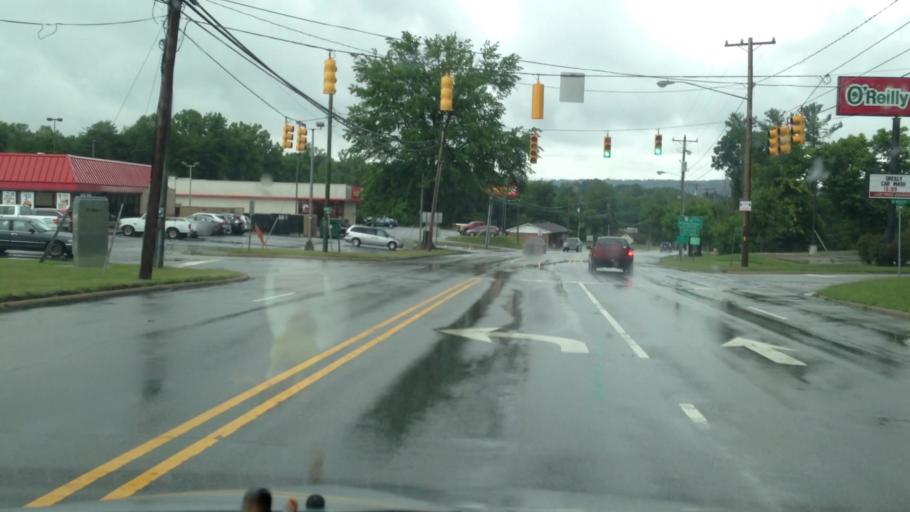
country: US
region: North Carolina
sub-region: Rockingham County
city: Mayodan
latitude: 36.4015
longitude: -79.9706
